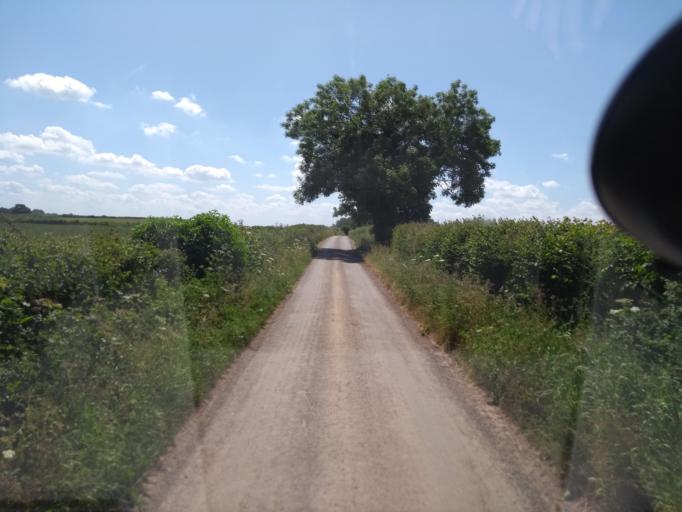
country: GB
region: England
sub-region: Somerset
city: North Petherton
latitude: 51.0554
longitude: -2.9995
